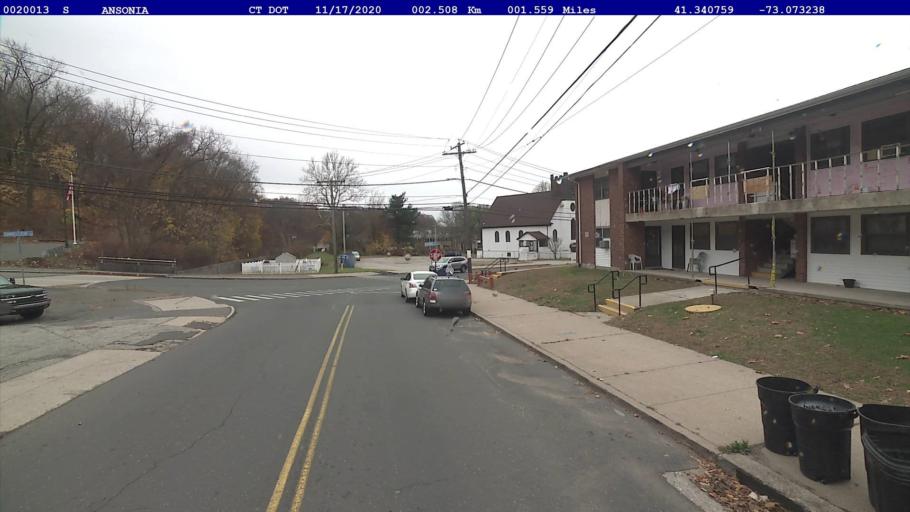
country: US
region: Connecticut
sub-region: New Haven County
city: Ansonia
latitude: 41.3408
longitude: -73.0732
